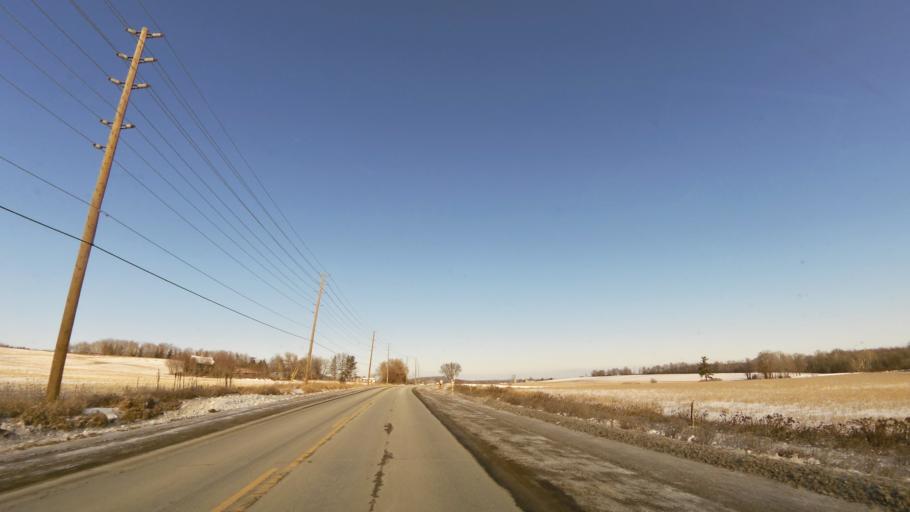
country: CA
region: Ontario
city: Quinte West
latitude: 44.1763
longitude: -77.8074
